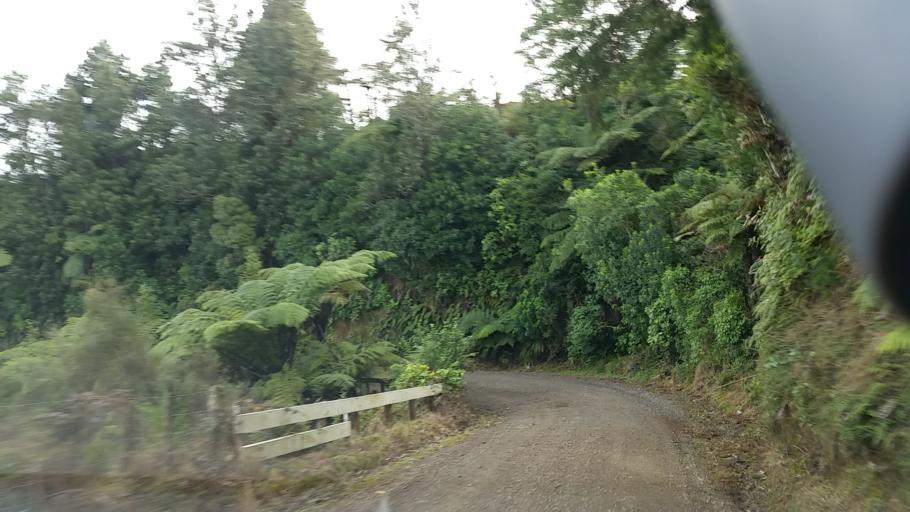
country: NZ
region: Taranaki
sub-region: New Plymouth District
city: Waitara
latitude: -39.0417
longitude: 174.4128
